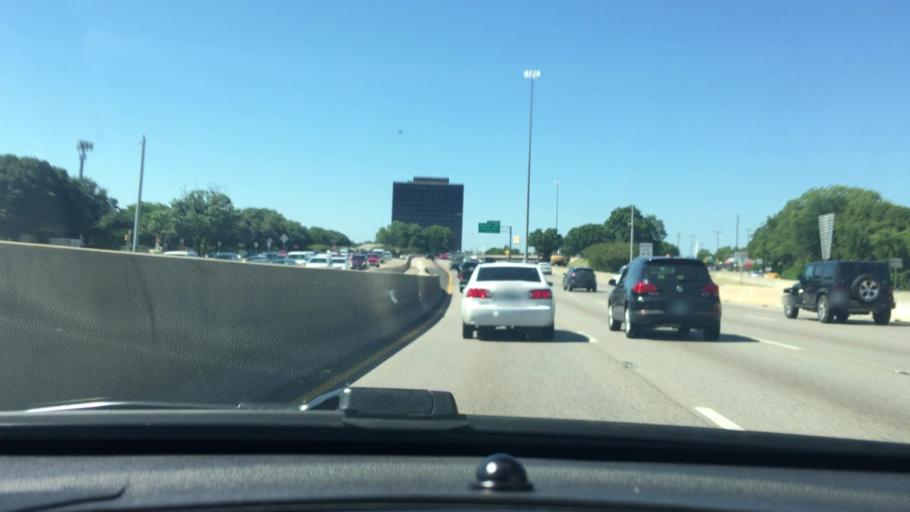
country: US
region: Texas
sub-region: Dallas County
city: Dallas
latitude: 32.7358
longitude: -96.8238
